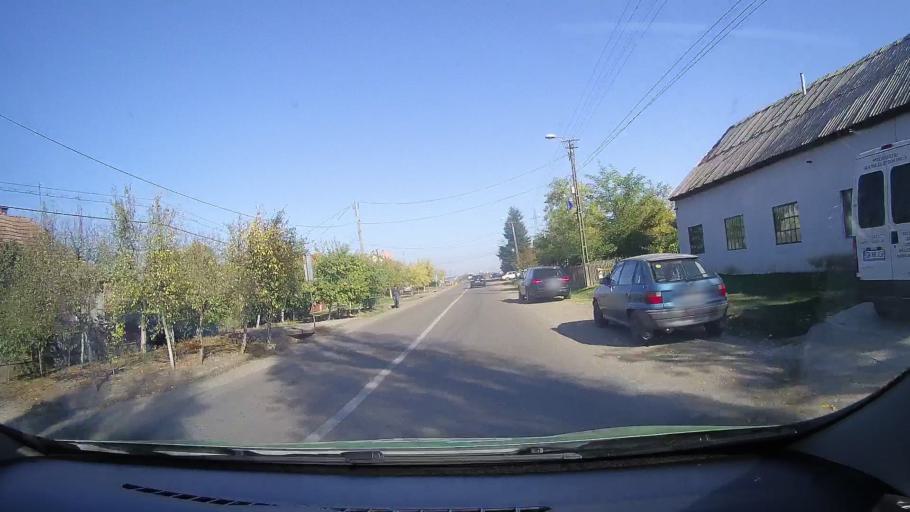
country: RO
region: Satu Mare
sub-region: Oras Tasnad
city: Tasnad
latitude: 47.4947
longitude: 22.5755
